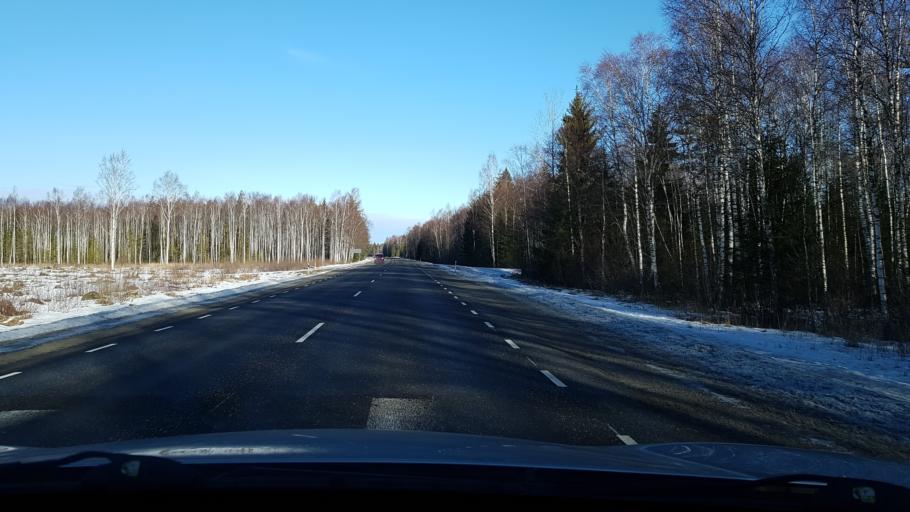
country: EE
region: Viljandimaa
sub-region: Vohma linn
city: Vohma
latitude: 58.6003
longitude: 25.5726
